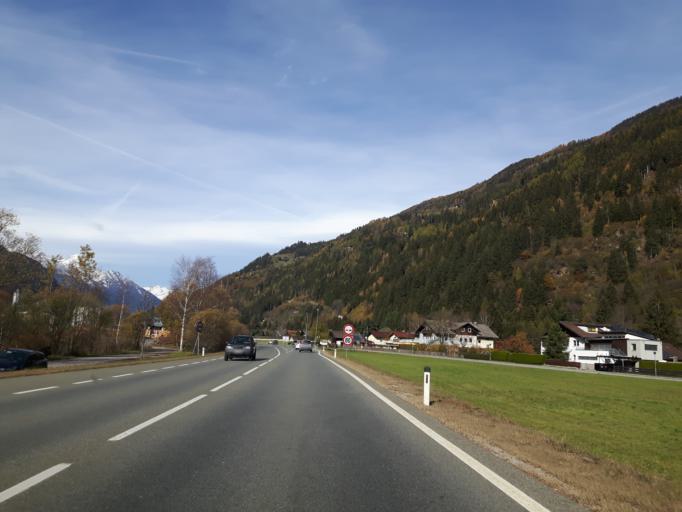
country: AT
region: Tyrol
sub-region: Politischer Bezirk Lienz
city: Ainet
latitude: 46.8691
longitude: 12.6848
